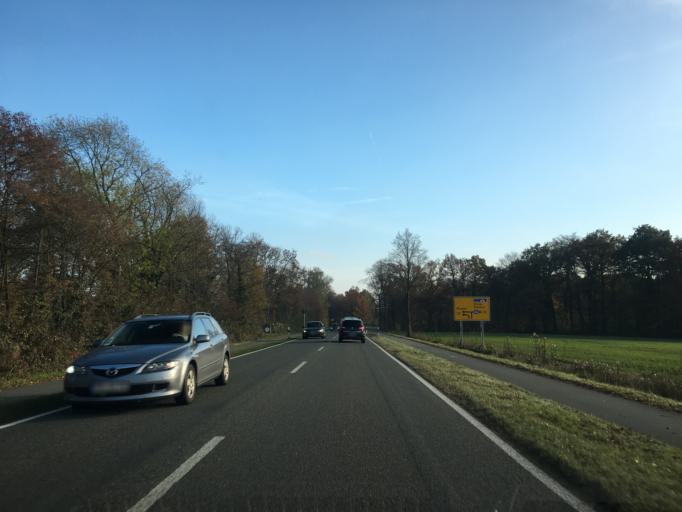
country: DE
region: North Rhine-Westphalia
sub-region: Regierungsbezirk Munster
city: Muenster
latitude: 51.9903
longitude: 7.5780
